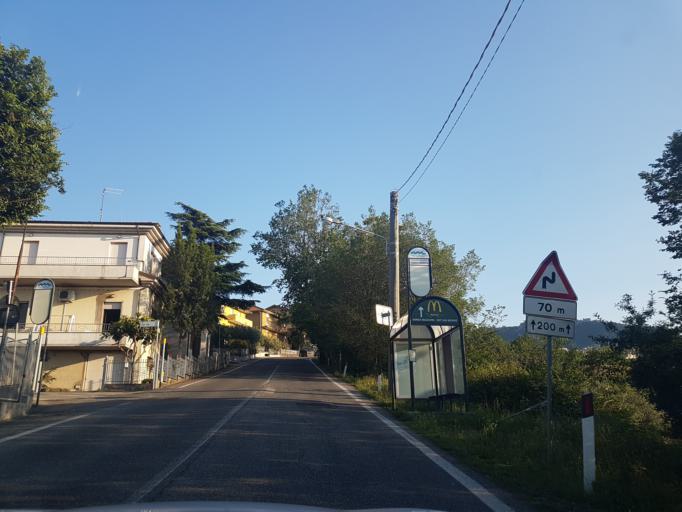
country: SM
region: Domagnano
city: Domagnano
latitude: 43.9616
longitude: 12.4690
